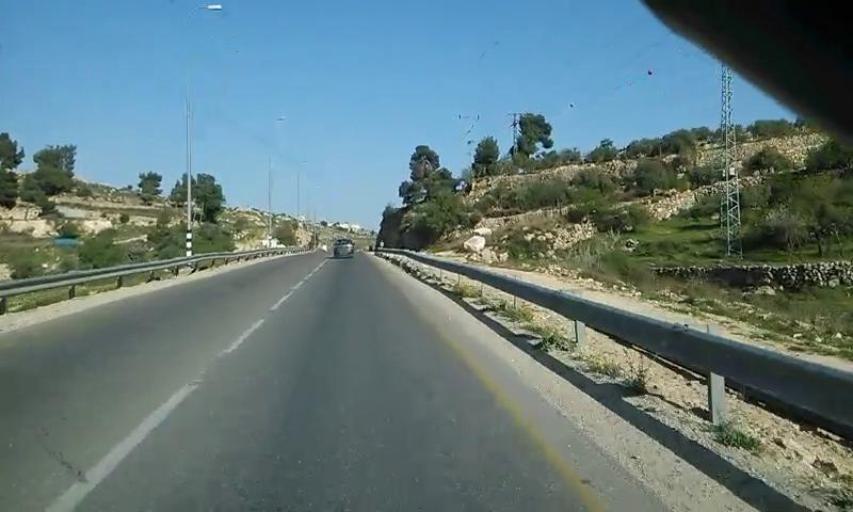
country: PS
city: Khallat ad Dar
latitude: 31.5047
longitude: 35.1311
